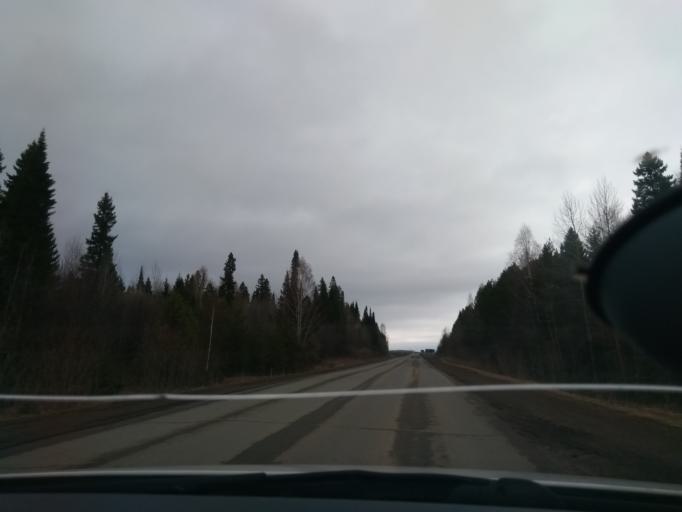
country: RU
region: Perm
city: Kungur
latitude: 57.3971
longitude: 56.8776
